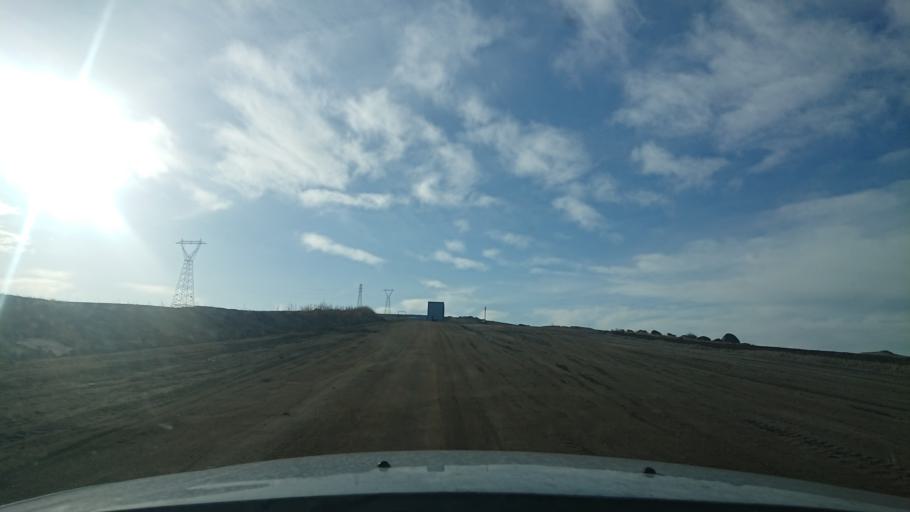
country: TR
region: Aksaray
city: Agacoren
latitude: 38.8499
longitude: 33.9429
